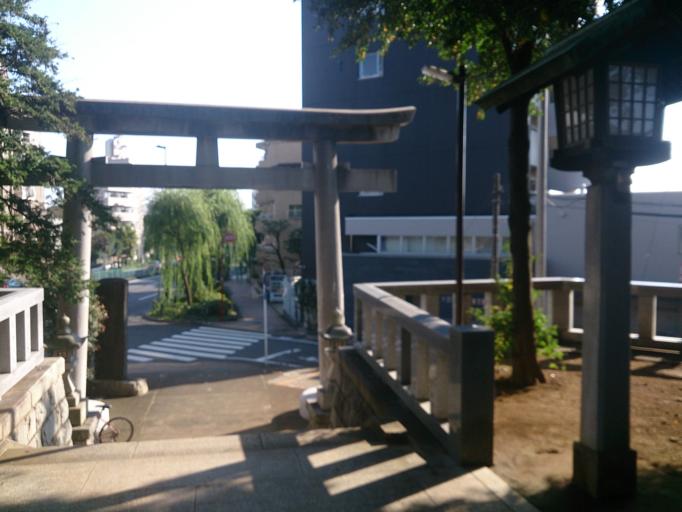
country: JP
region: Tokyo
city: Tokyo
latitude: 35.6571
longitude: 139.6598
